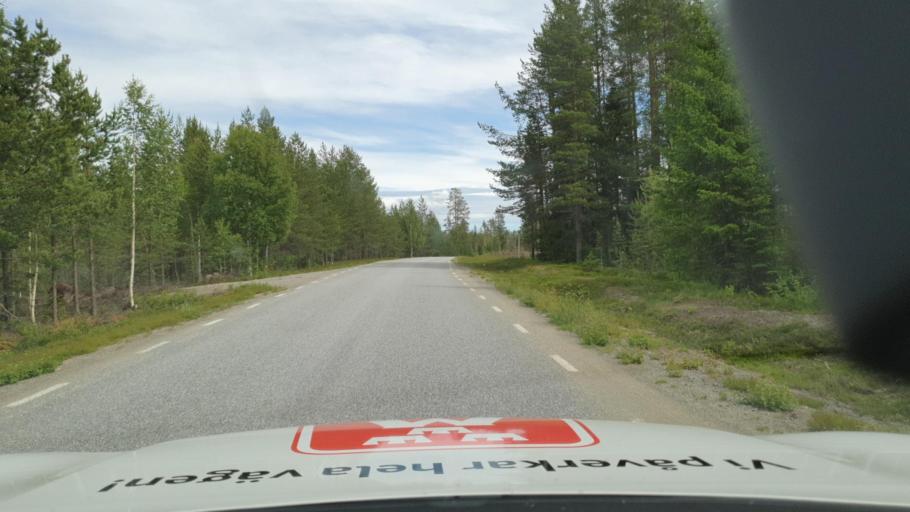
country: SE
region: Vaesterbotten
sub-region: Skelleftea Kommun
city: Burtraesk
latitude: 64.5029
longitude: 20.8314
